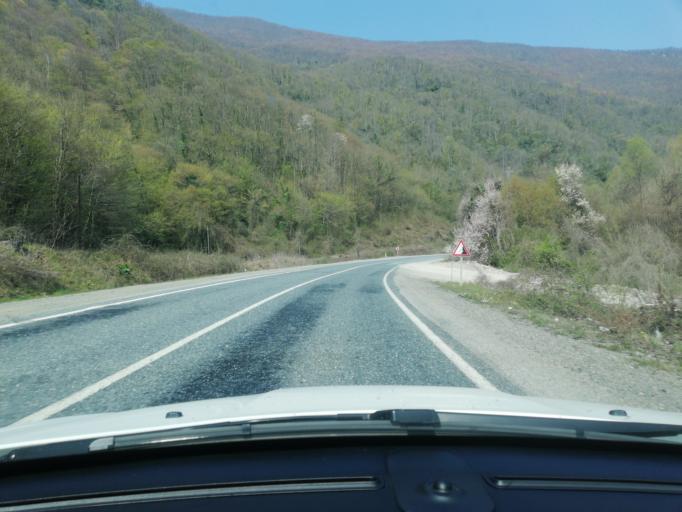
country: TR
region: Zonguldak
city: Gokcebey
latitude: 41.2645
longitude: 32.1580
